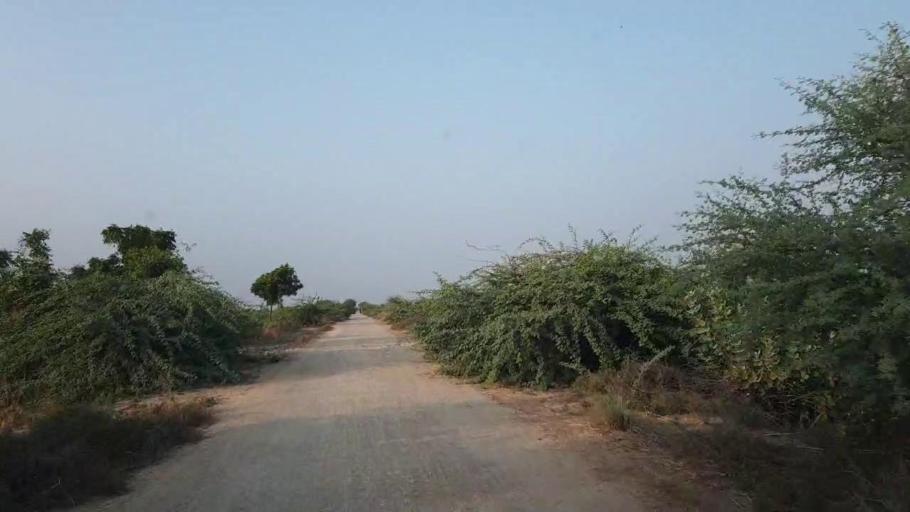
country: PK
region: Sindh
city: Rajo Khanani
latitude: 25.0265
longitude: 68.9772
